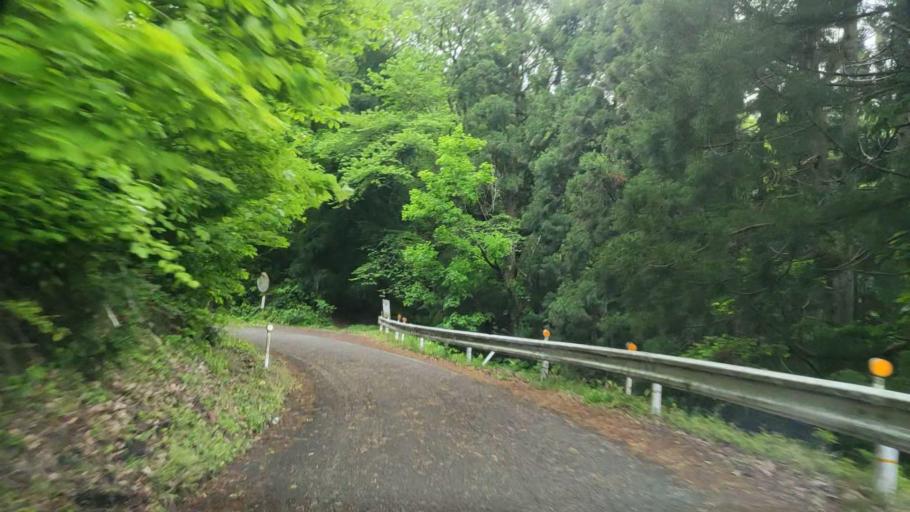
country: JP
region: Niigata
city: Kamo
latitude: 37.7157
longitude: 139.0898
